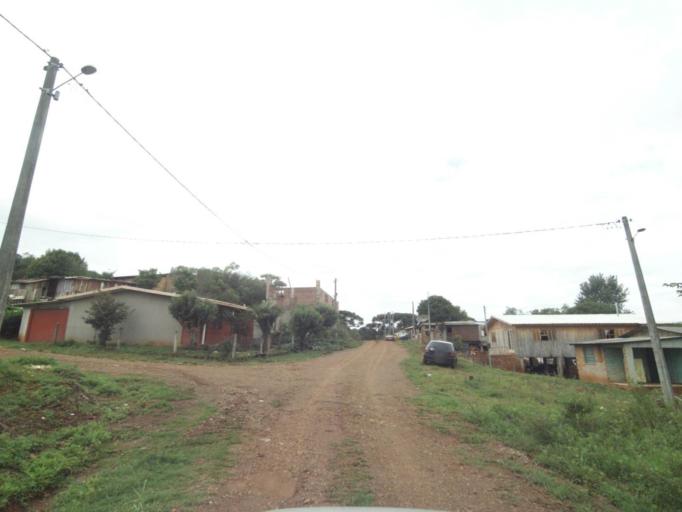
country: BR
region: Rio Grande do Sul
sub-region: Lagoa Vermelha
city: Lagoa Vermelha
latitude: -28.2258
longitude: -51.5412
